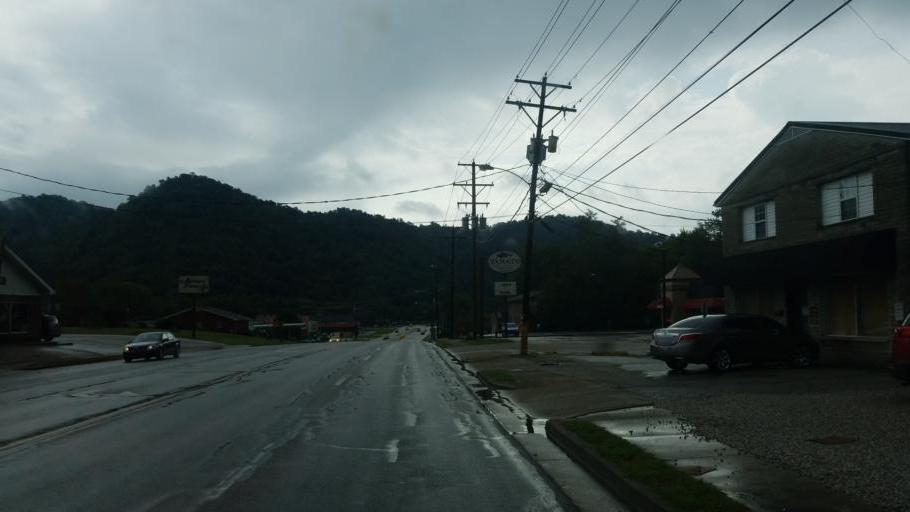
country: US
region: Kentucky
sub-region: Rowan County
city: Morehead
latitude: 38.1785
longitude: -83.4402
